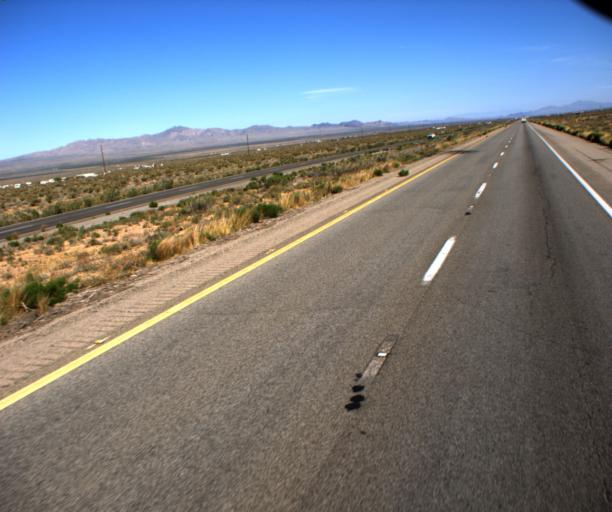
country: US
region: Arizona
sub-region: Mohave County
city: Dolan Springs
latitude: 35.4845
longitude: -114.3210
